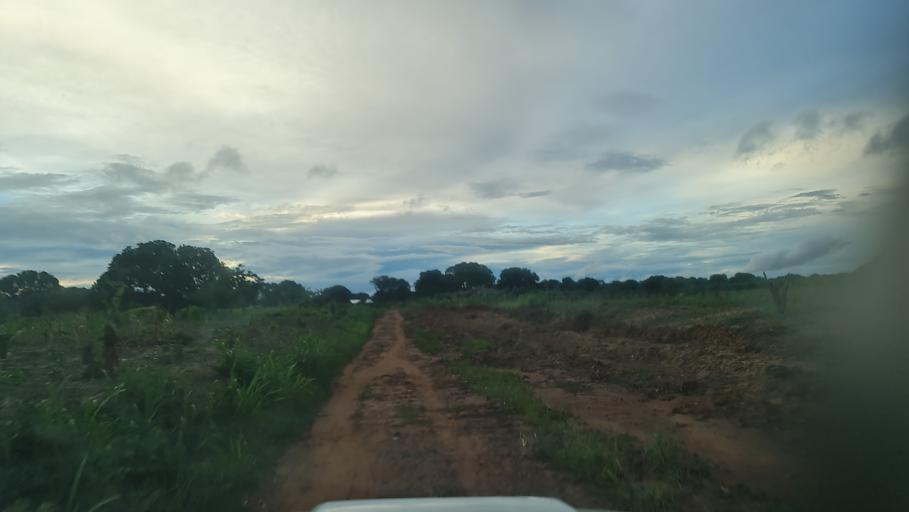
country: MZ
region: Nampula
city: Nacala
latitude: -14.7410
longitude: 39.9445
